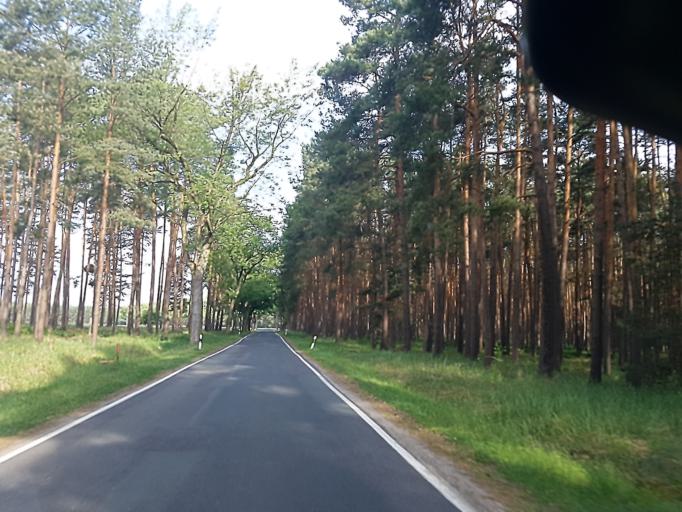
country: DE
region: Brandenburg
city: Belzig
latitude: 52.0706
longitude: 12.5558
